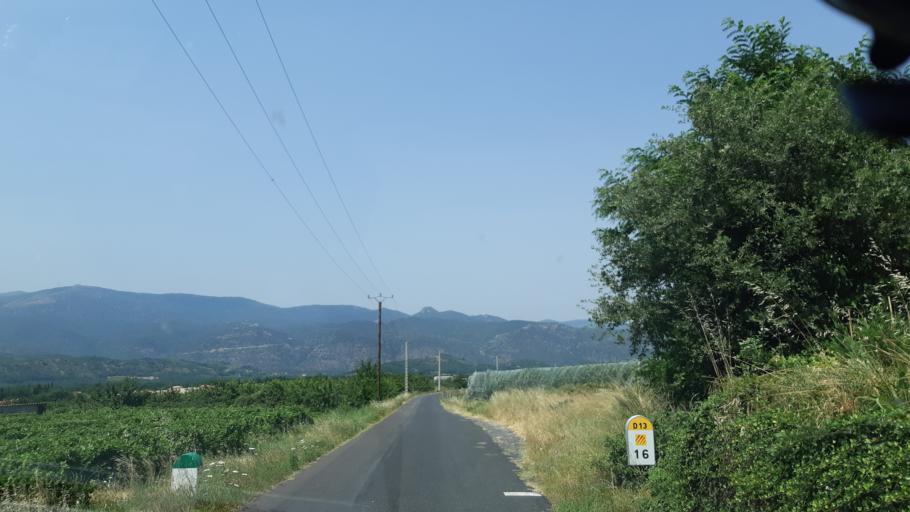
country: FR
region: Languedoc-Roussillon
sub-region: Departement des Pyrenees-Orientales
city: Vinca
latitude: 42.6143
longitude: 2.5174
